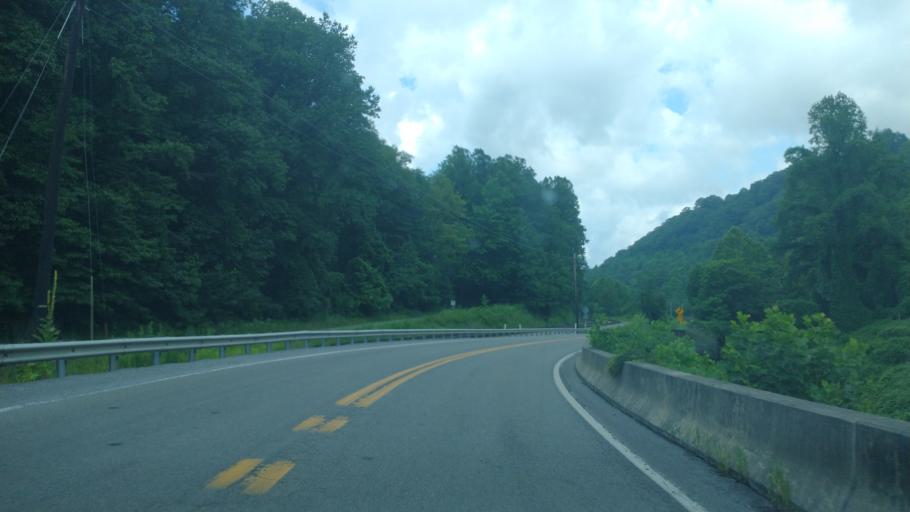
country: US
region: West Virginia
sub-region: McDowell County
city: Welch
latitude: 37.4108
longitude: -81.4717
